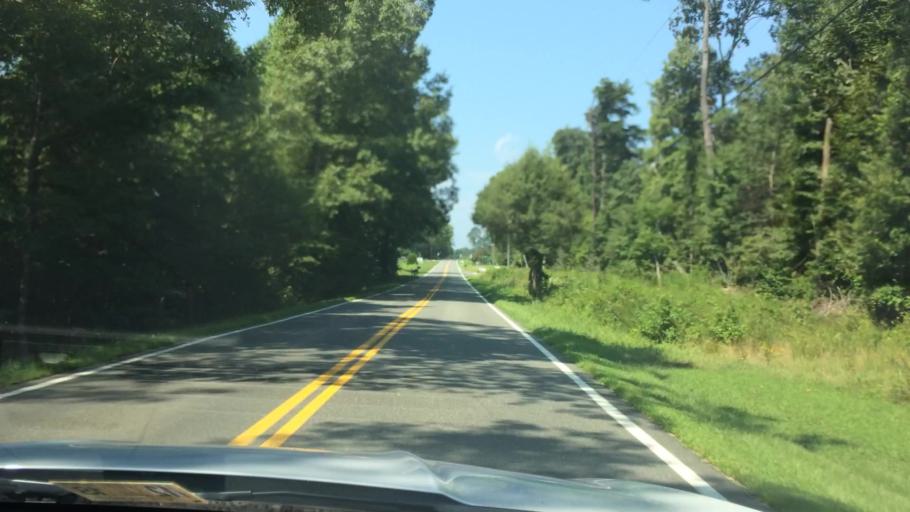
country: US
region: Virginia
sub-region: New Kent County
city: New Kent
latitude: 37.5261
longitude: -77.0348
